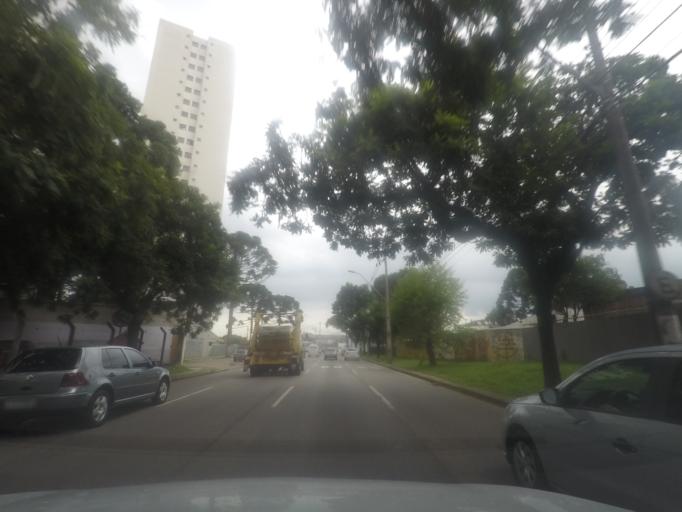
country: BR
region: Parana
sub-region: Curitiba
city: Curitiba
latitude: -25.4981
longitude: -49.2971
